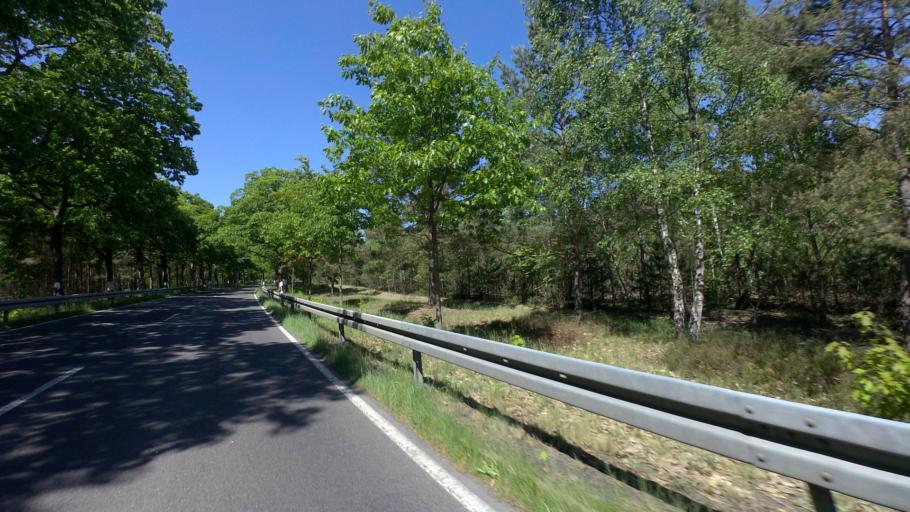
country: DE
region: Brandenburg
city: Drehnow
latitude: 51.8999
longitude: 14.3578
